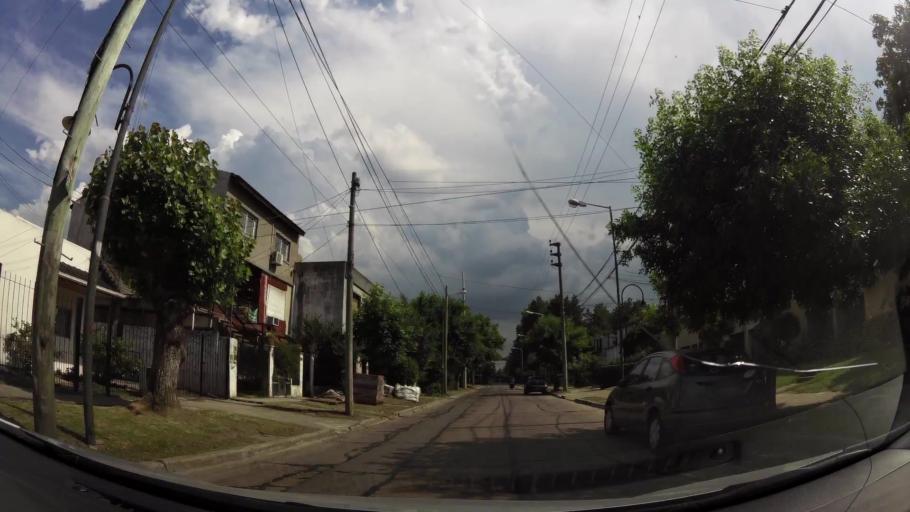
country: AR
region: Buenos Aires
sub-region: Partido de Tigre
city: Tigre
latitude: -34.4668
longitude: -58.5754
